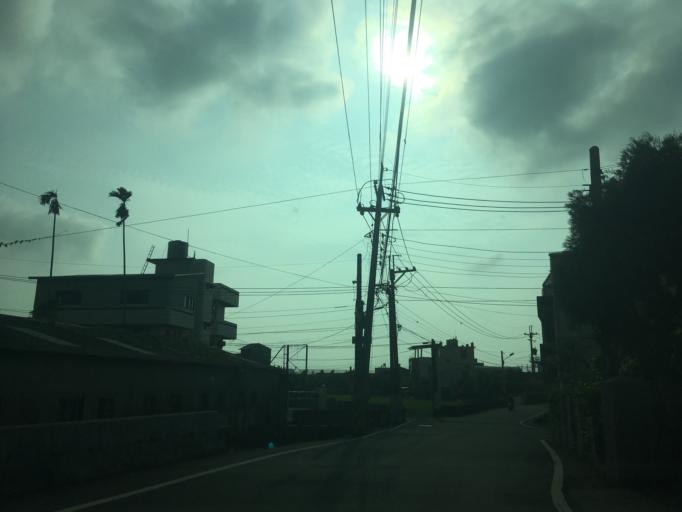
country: TW
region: Taiwan
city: Fengyuan
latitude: 24.2287
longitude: 120.7273
